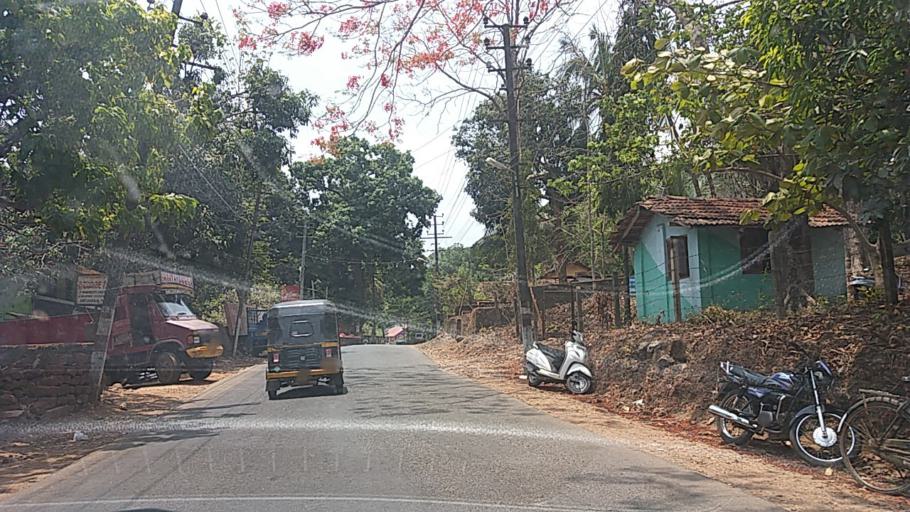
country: IN
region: Karnataka
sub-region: Uttar Kannada
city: Karwar
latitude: 14.8113
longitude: 74.1542
